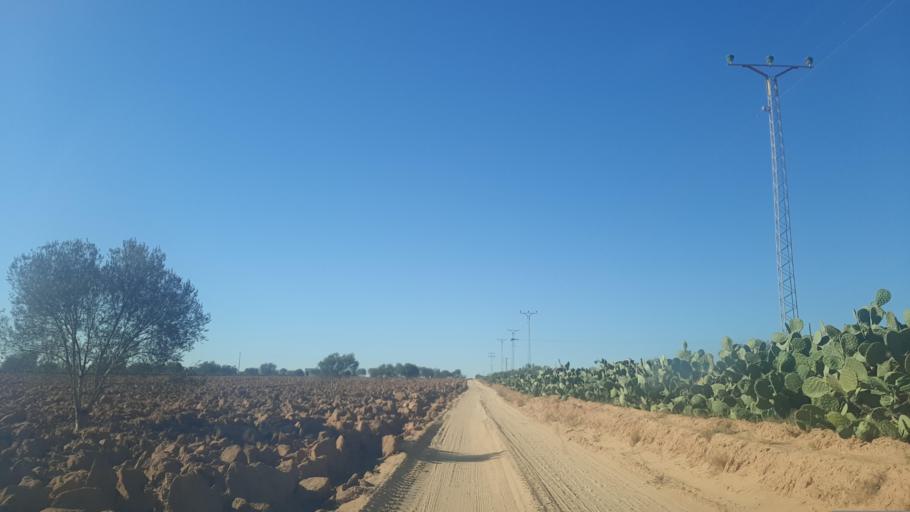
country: TN
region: Safaqis
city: Sfax
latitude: 34.8916
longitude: 10.5924
